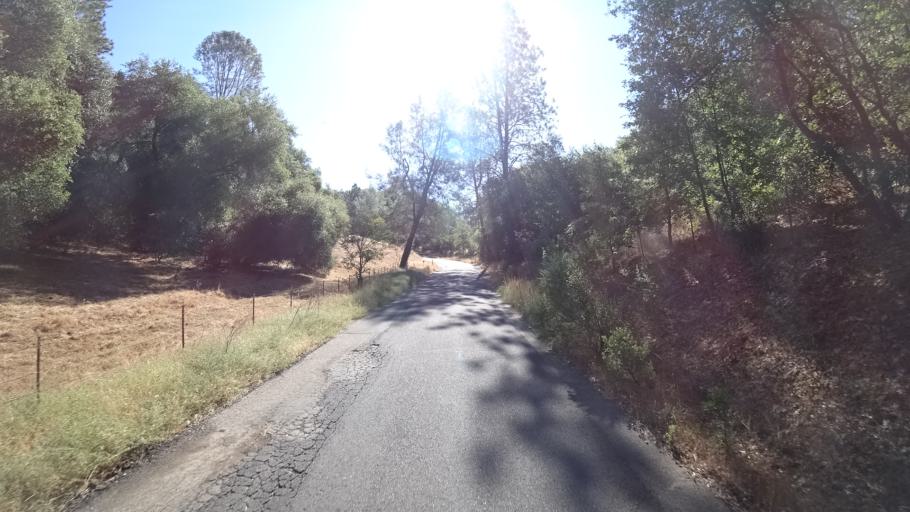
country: US
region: California
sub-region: Calaveras County
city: San Andreas
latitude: 38.2298
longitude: -120.6647
